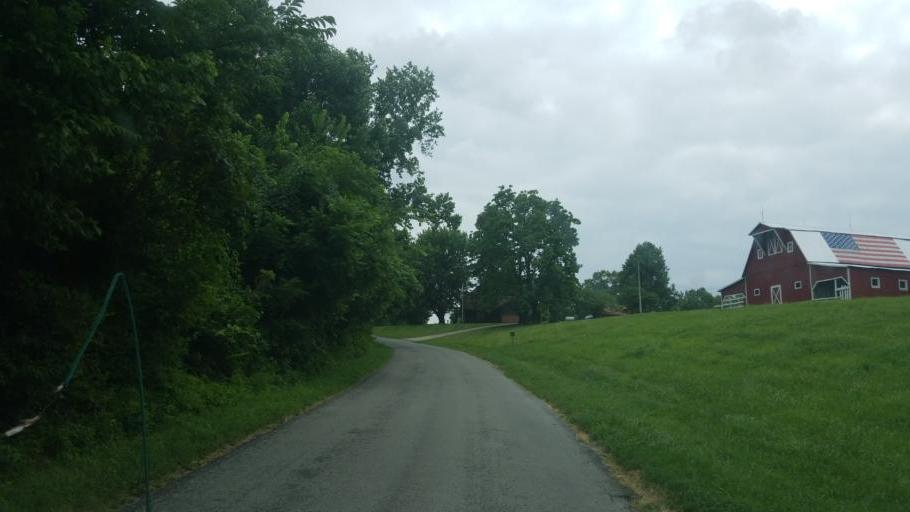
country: US
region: Illinois
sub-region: Jackson County
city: Murphysboro
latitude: 37.6896
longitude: -89.3881
